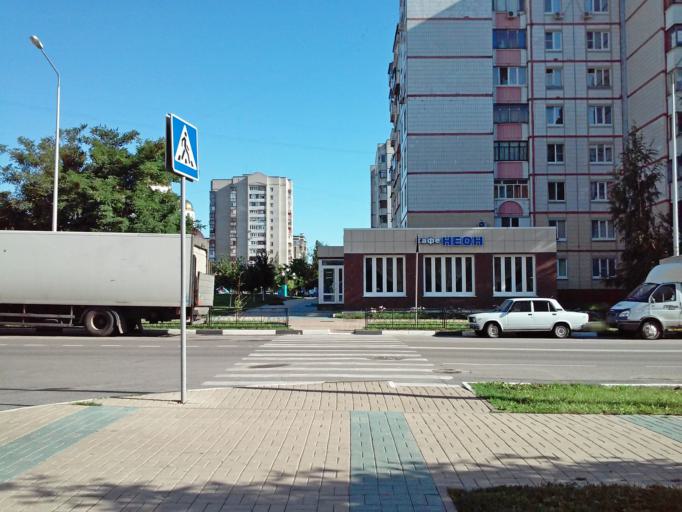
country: RU
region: Belgorod
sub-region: Belgorodskiy Rayon
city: Belgorod
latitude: 50.5598
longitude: 36.5674
